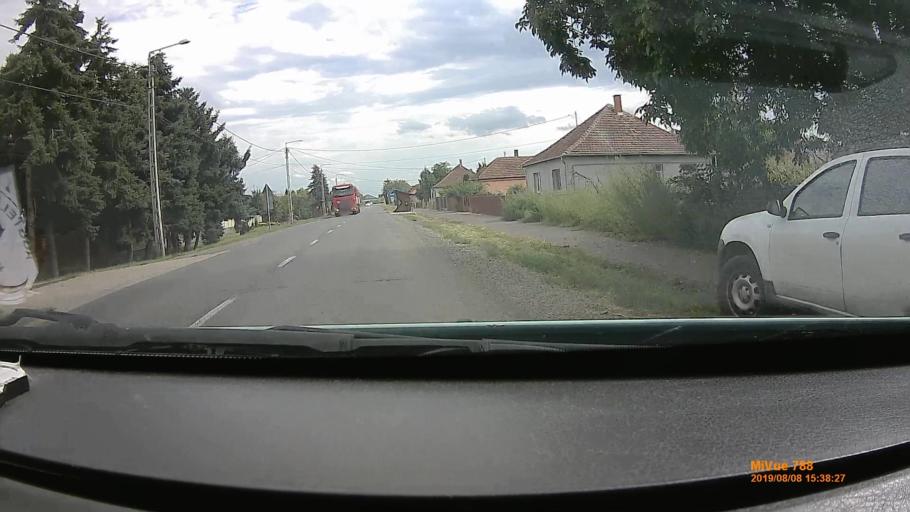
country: HU
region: Szabolcs-Szatmar-Bereg
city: Kocsord
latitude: 47.9423
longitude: 22.4280
